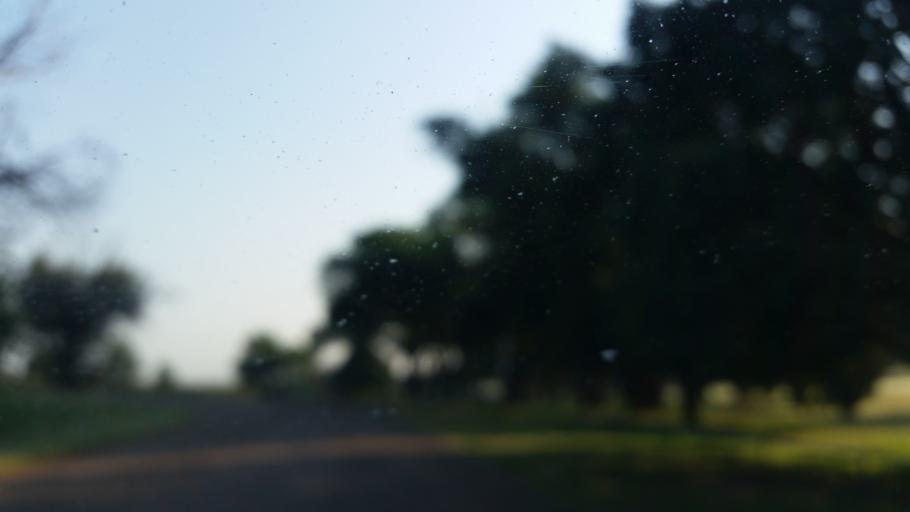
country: US
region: New Mexico
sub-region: Curry County
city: Clovis
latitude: 34.5210
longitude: -103.1947
